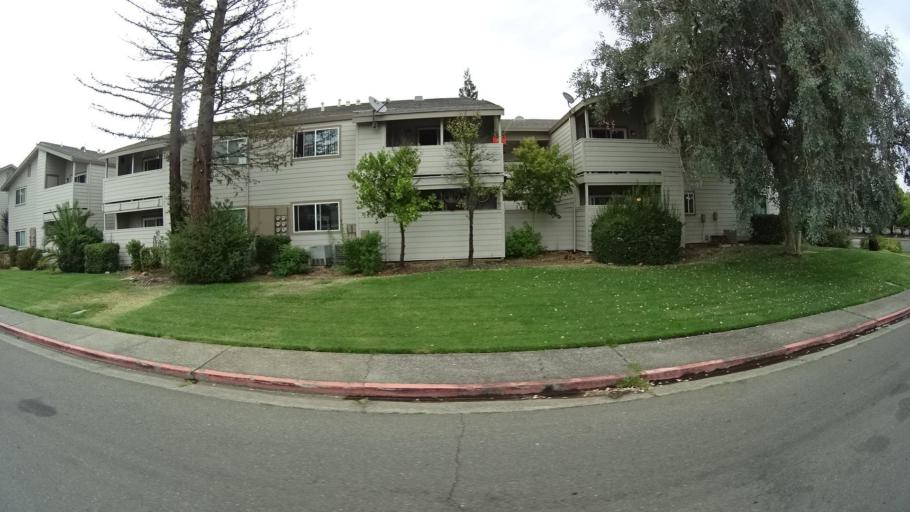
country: US
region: California
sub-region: Placer County
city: Rocklin
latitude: 38.7837
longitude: -121.2496
